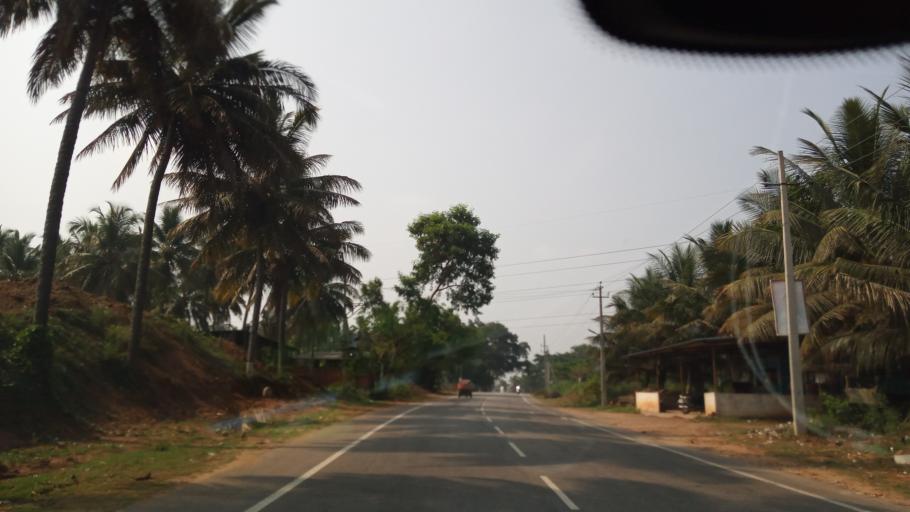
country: IN
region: Karnataka
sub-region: Mandya
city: Pandavapura
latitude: 12.5152
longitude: 76.6744
